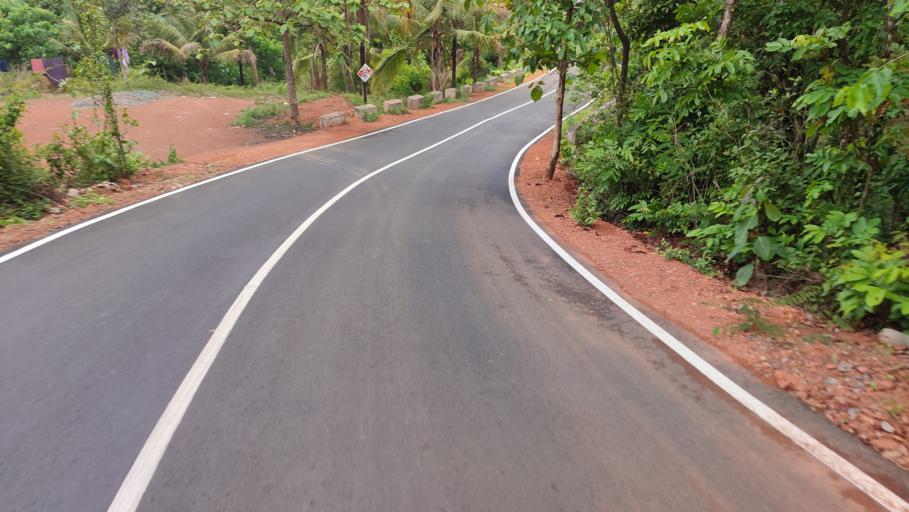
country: IN
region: Kerala
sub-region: Kasaragod District
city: Kannangad
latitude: 12.3215
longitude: 75.1541
